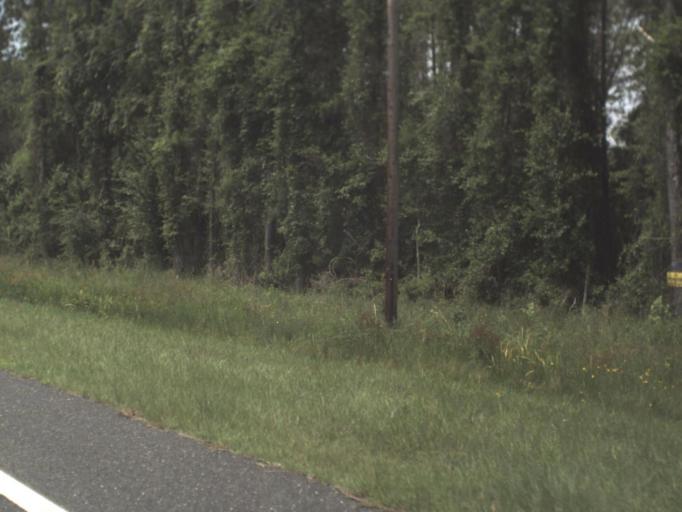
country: US
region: Florida
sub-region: Levy County
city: Chiefland
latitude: 29.3497
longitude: -82.7823
